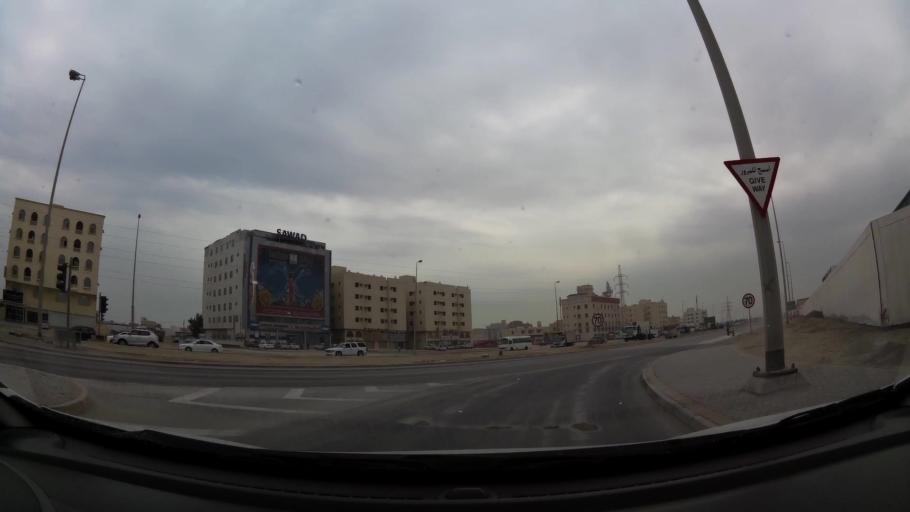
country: BH
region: Northern
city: Sitrah
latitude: 26.1761
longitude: 50.6044
